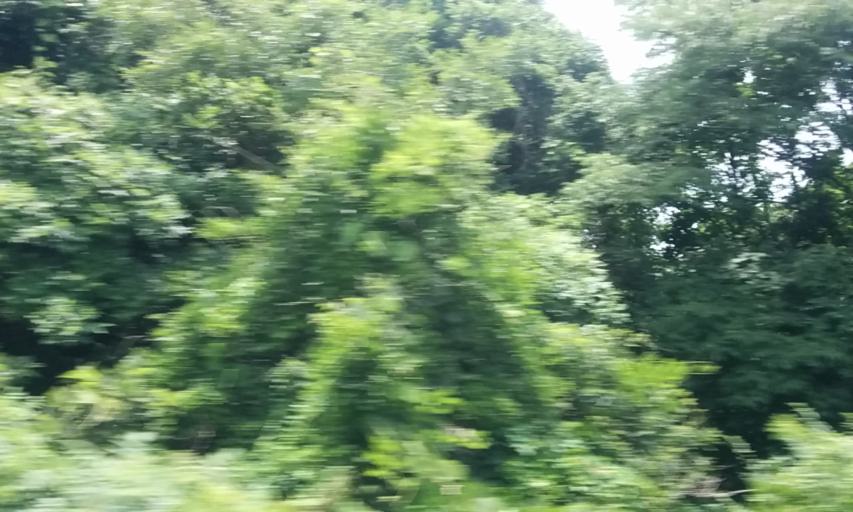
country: JP
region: Chiba
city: Narita
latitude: 35.8354
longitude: 140.3446
